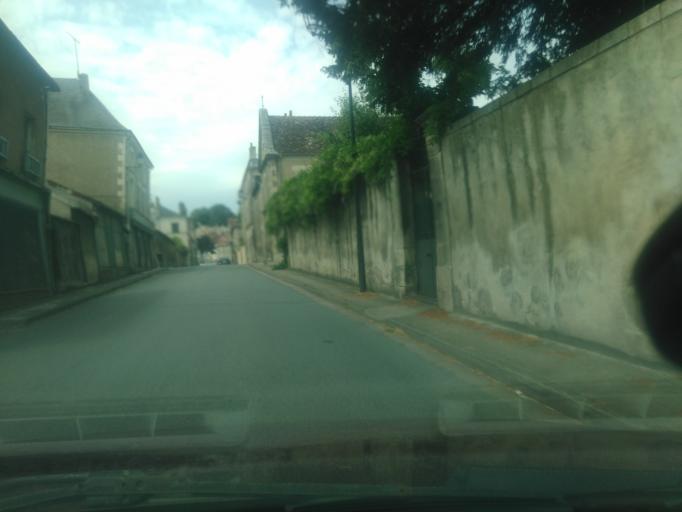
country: FR
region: Poitou-Charentes
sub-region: Departement de la Vienne
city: Saint-Savin
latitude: 46.5655
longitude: 0.8662
